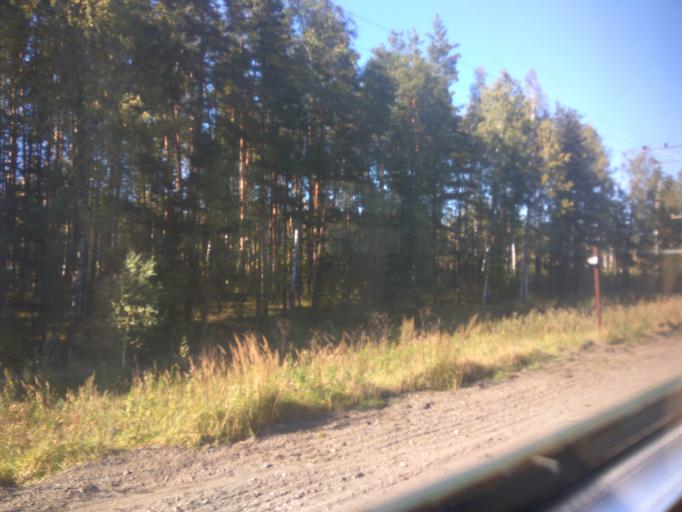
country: RU
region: Moskovskaya
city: Kurovskoye
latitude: 55.5567
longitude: 38.8784
